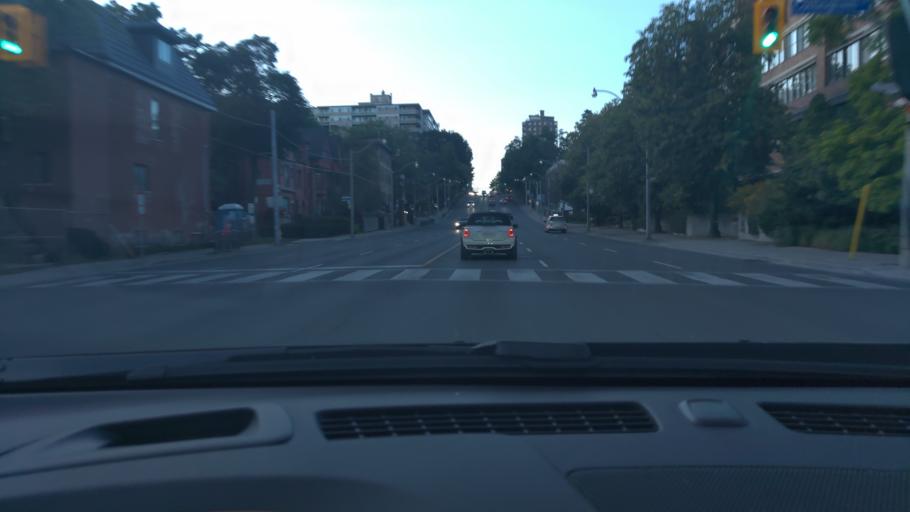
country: CA
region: Ontario
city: Toronto
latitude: 43.6795
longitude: -79.3985
